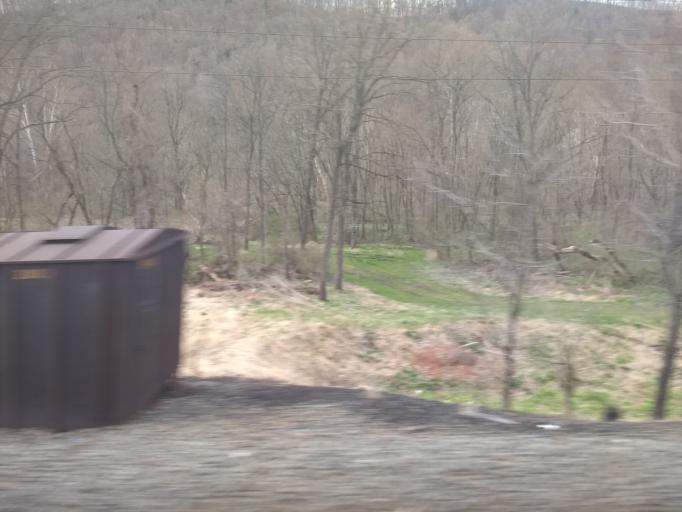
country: US
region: Pennsylvania
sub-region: Huntingdon County
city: Huntingdon
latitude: 40.4628
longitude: -77.9820
